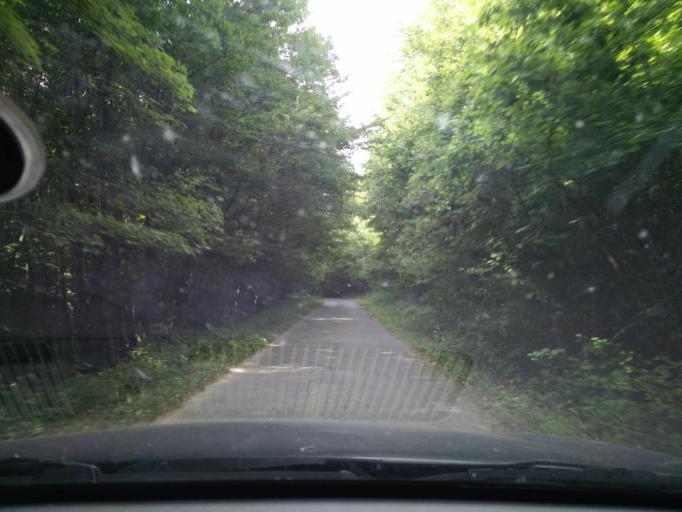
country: HU
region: Komarom-Esztergom
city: Tardos
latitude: 47.7090
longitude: 18.4625
